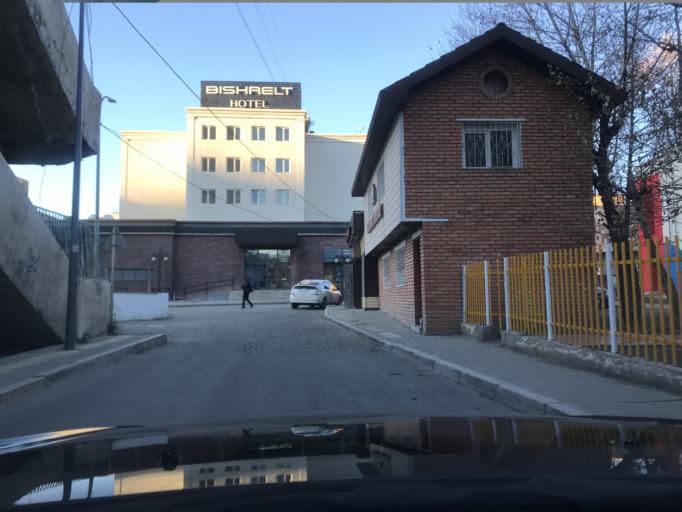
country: MN
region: Ulaanbaatar
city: Ulaanbaatar
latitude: 47.9230
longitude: 106.9072
